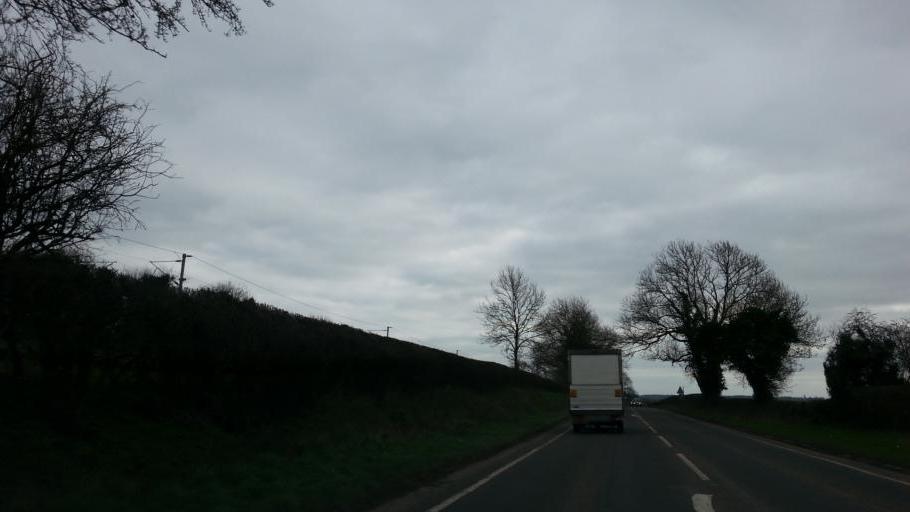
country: GB
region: England
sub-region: Staffordshire
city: Stone
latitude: 52.8849
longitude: -2.1189
